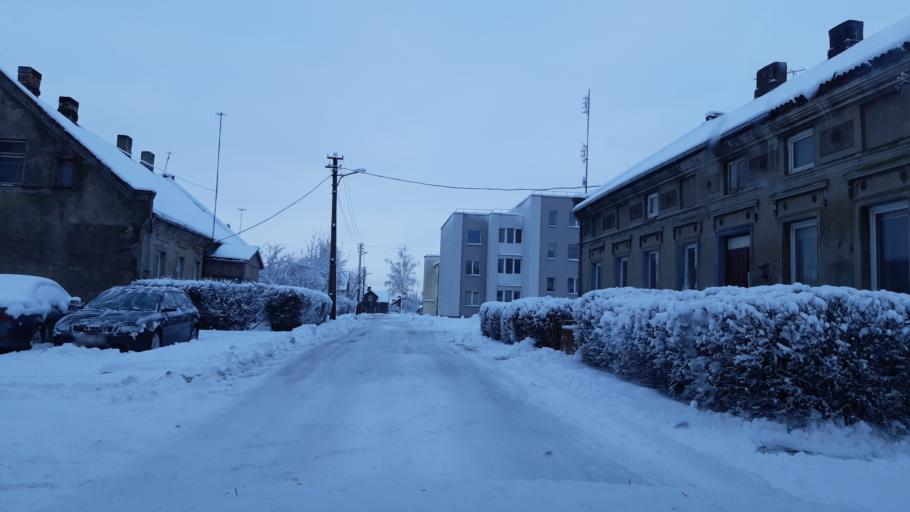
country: LT
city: Kybartai
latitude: 54.6354
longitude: 22.7562
